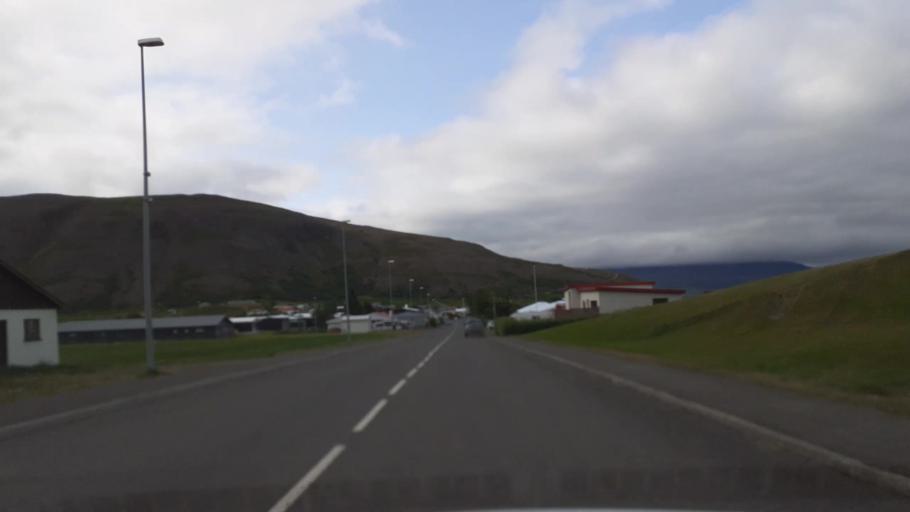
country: IS
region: Northeast
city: Akureyri
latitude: 65.9518
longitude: -18.1785
